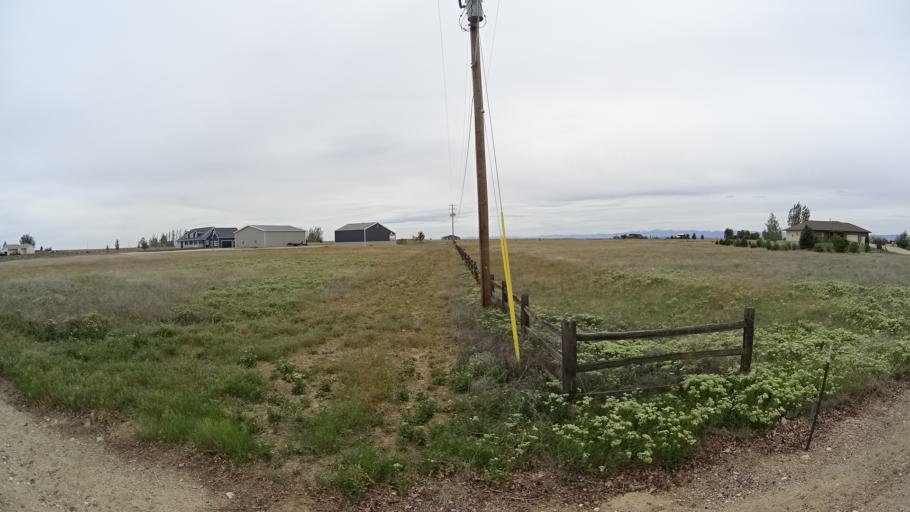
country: US
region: Idaho
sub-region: Ada County
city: Kuna
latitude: 43.4885
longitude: -116.3003
